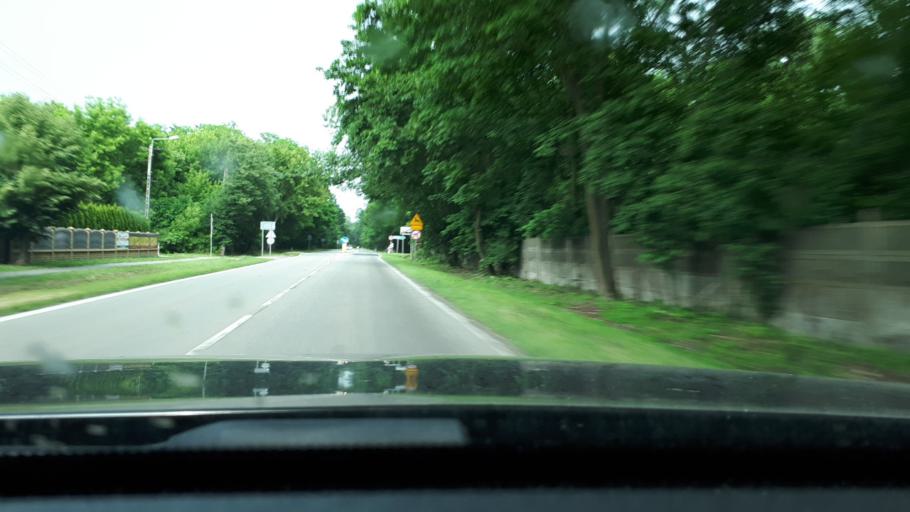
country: PL
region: Masovian Voivodeship
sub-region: Powiat warszawski zachodni
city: Leszno
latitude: 52.2630
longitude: 20.6509
